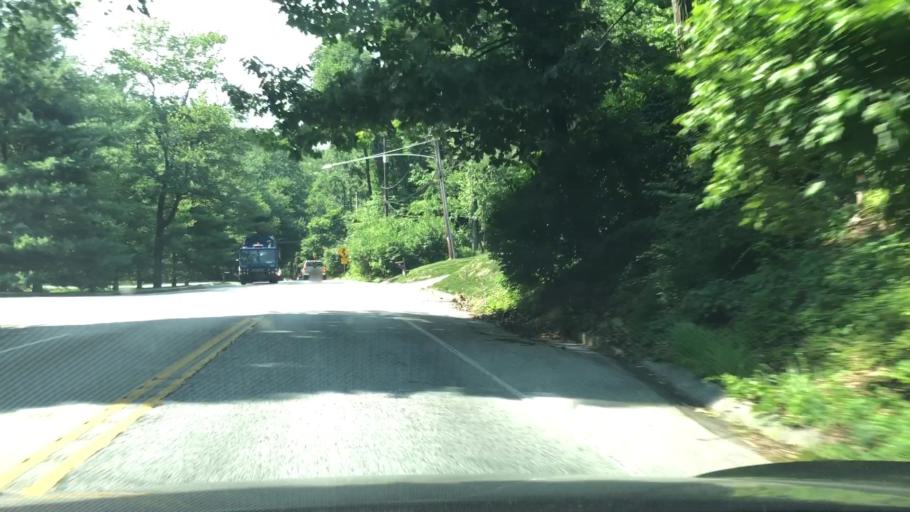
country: US
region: Pennsylvania
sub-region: Chester County
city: Devon
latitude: 40.0561
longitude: -75.4300
